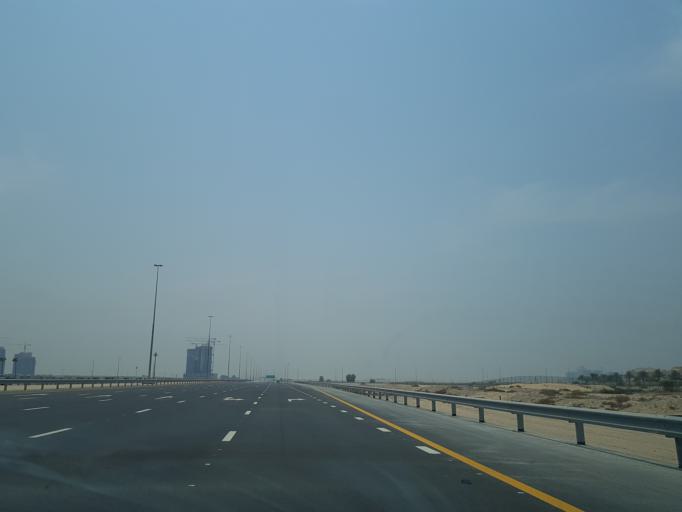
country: AE
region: Dubai
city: Dubai
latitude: 25.0324
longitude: 55.2540
